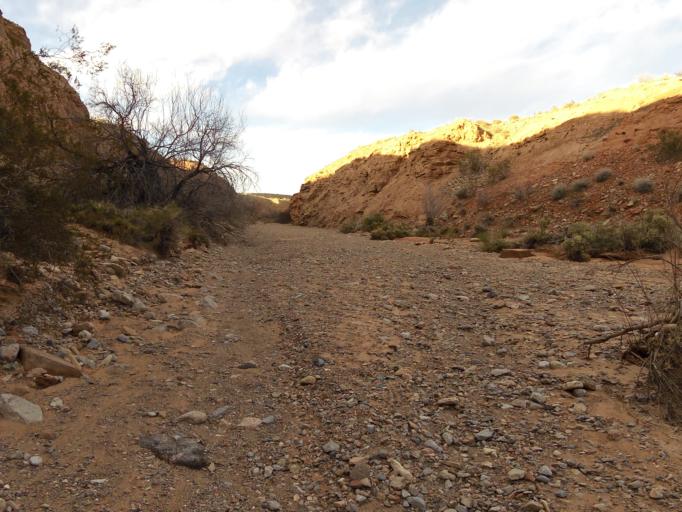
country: US
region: Nevada
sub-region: Clark County
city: Boulder City
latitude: 36.2435
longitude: -114.6326
